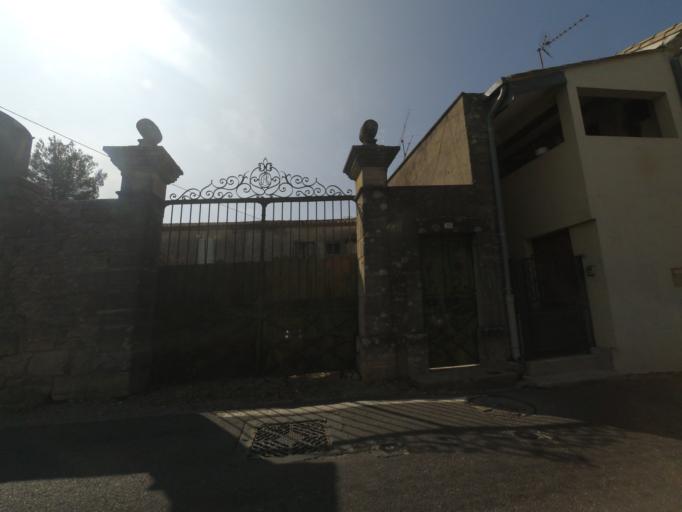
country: FR
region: Languedoc-Roussillon
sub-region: Departement du Gard
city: Villevieille
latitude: 43.8127
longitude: 4.1217
